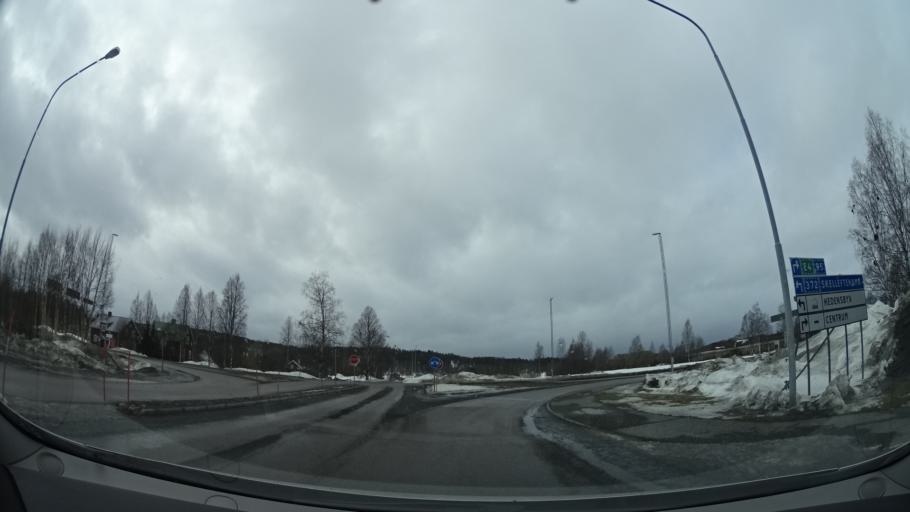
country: SE
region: Vaesterbotten
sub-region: Skelleftea Kommun
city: Skelleftea
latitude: 64.7464
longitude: 21.0140
